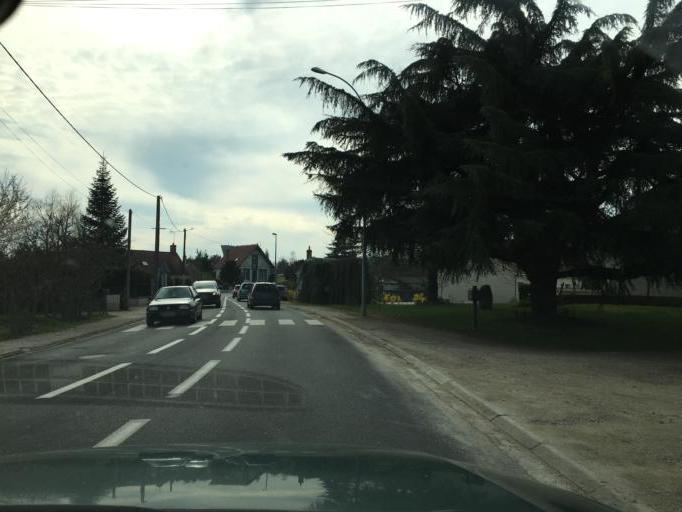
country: FR
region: Centre
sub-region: Departement du Loiret
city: Vienne-en-Val
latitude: 47.8014
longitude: 2.1400
